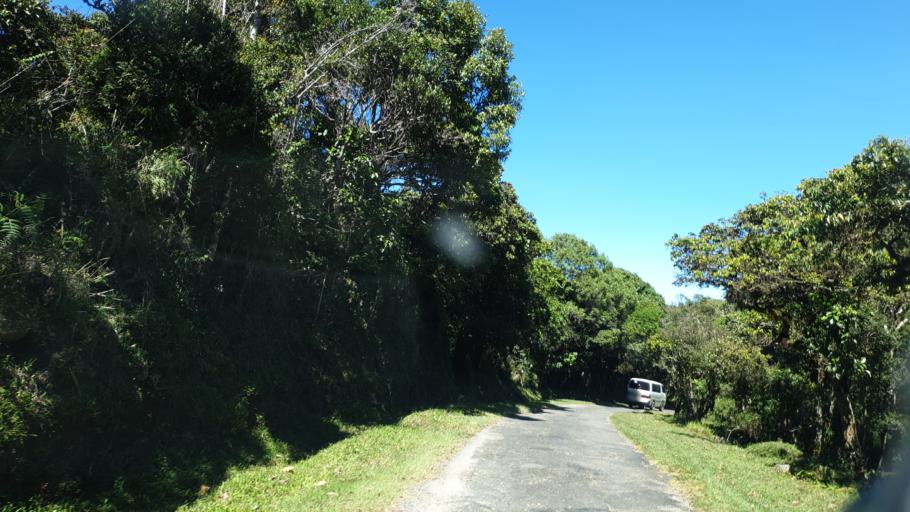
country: LK
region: Uva
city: Haputale
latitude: 6.8027
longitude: 80.8330
